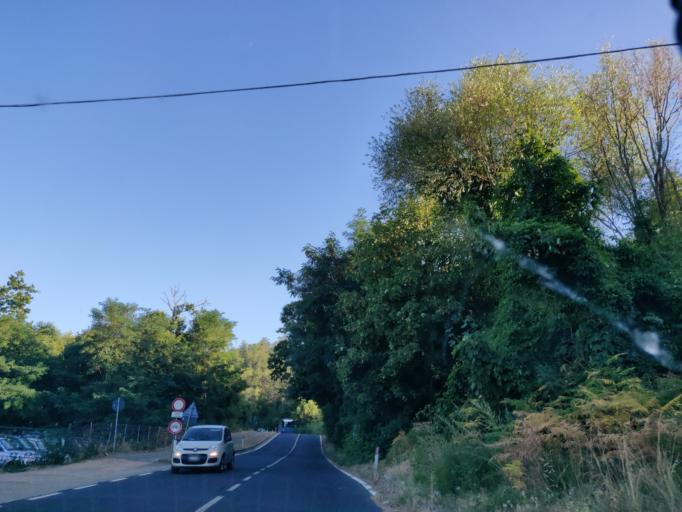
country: IT
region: Tuscany
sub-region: Provincia di Siena
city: Piancastagnaio
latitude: 42.8627
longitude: 11.6787
